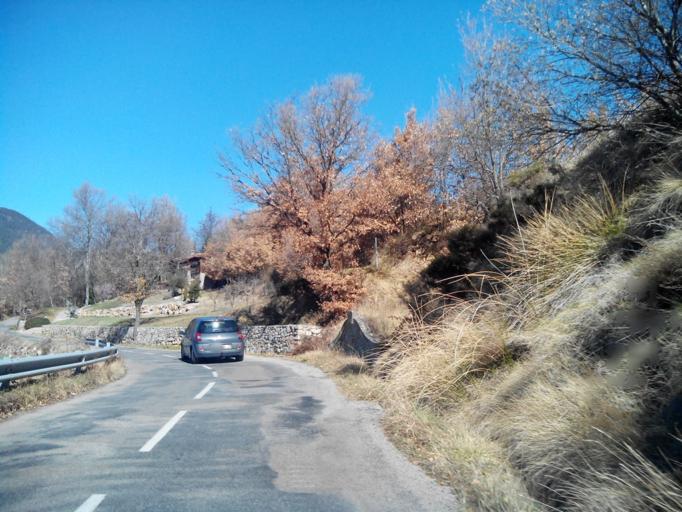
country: ES
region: Catalonia
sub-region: Provincia de Lleida
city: Lles de Cerdanya
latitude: 42.3783
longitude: 1.6867
